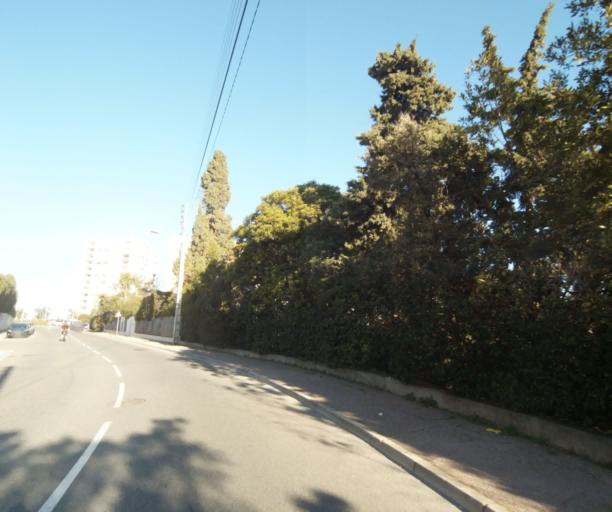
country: FR
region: Provence-Alpes-Cote d'Azur
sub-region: Departement des Alpes-Maritimes
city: Antibes
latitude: 43.5825
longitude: 7.1099
